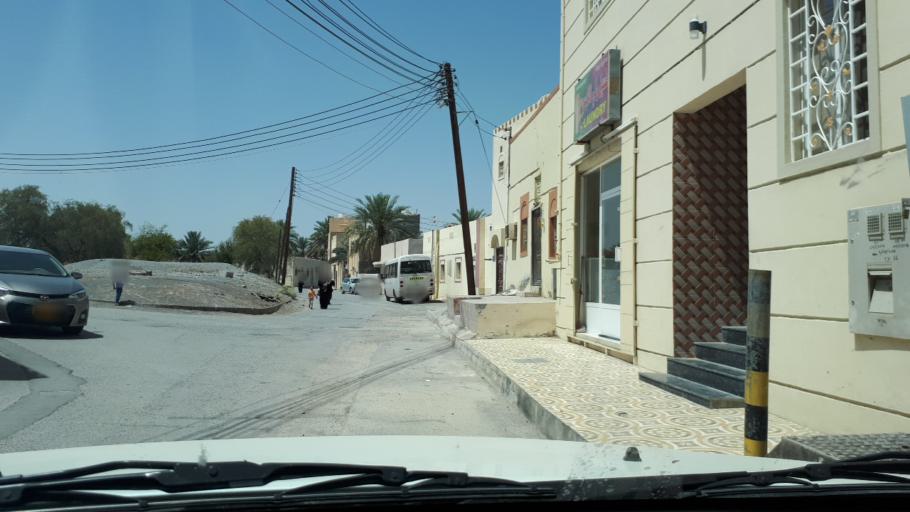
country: OM
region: Muhafazat ad Dakhiliyah
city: Nizwa
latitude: 22.9266
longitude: 57.5315
